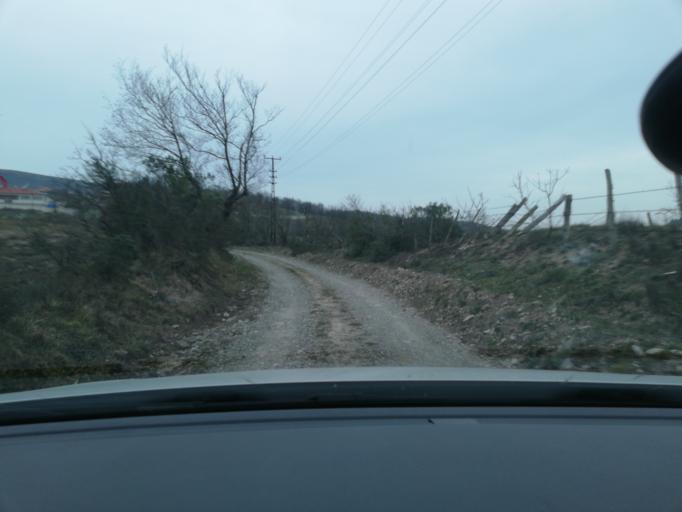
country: TR
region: Zonguldak
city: Saltukova
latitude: 41.5177
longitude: 32.0739
